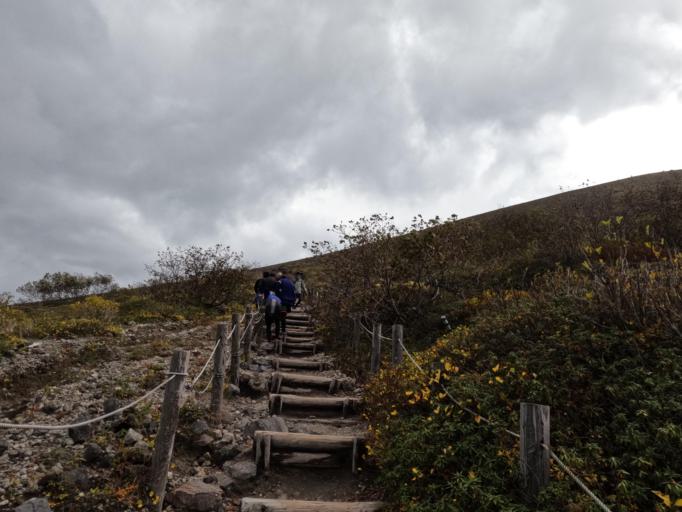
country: JP
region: Hokkaido
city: Shiraoi
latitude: 42.6951
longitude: 141.3901
